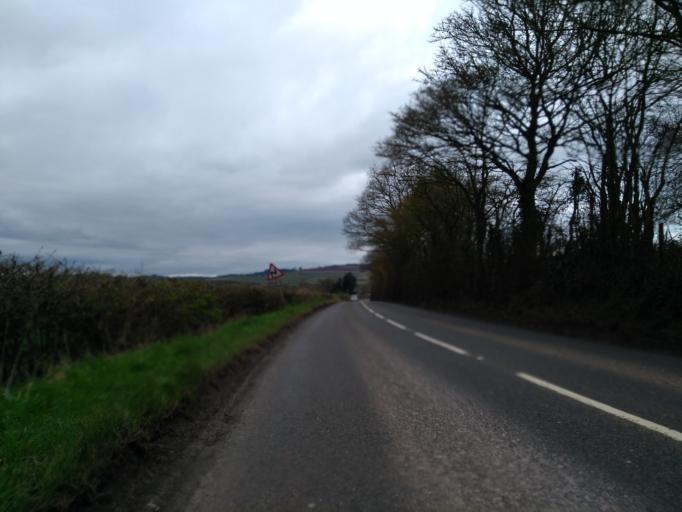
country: GB
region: England
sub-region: Devon
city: Heavitree
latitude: 50.7953
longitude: -3.4956
